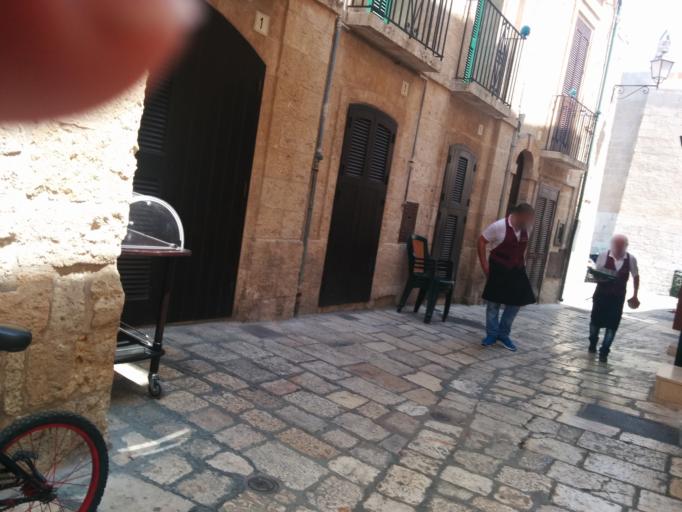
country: IT
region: Apulia
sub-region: Provincia di Bari
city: Polignano a Mare
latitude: 40.9968
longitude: 17.2194
